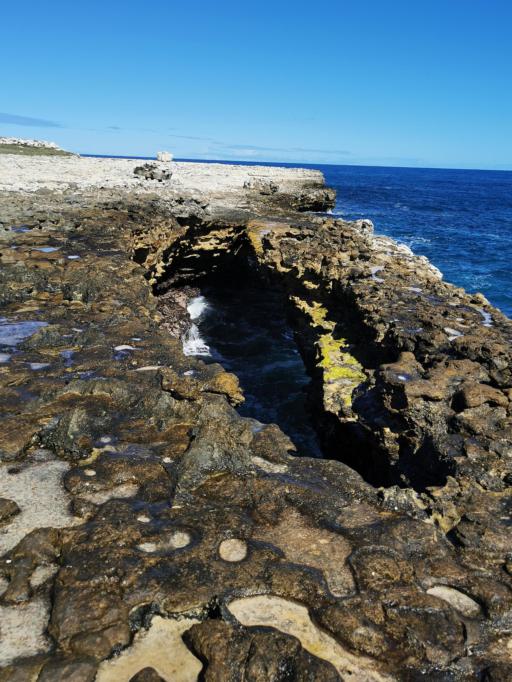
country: AG
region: Saint Peter
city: Parham
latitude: 17.1004
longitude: -61.6785
